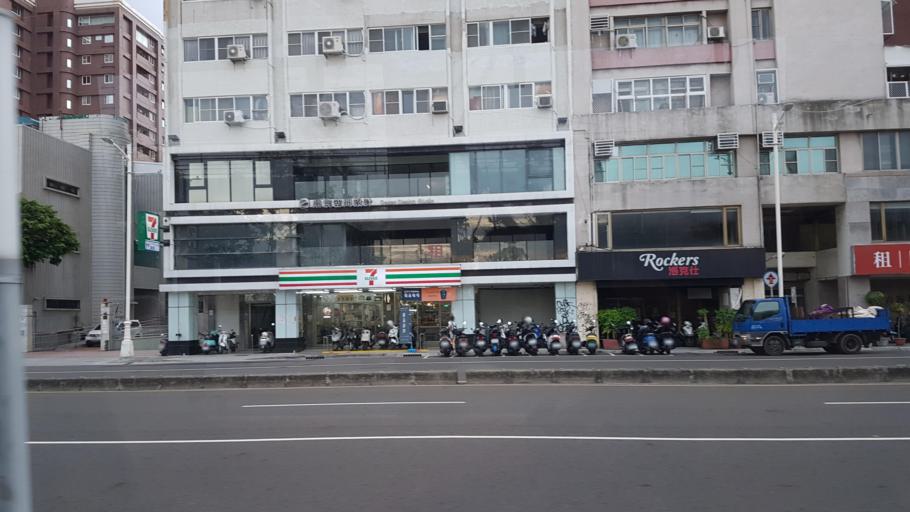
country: TW
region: Kaohsiung
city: Kaohsiung
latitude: 22.6179
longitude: 120.2935
